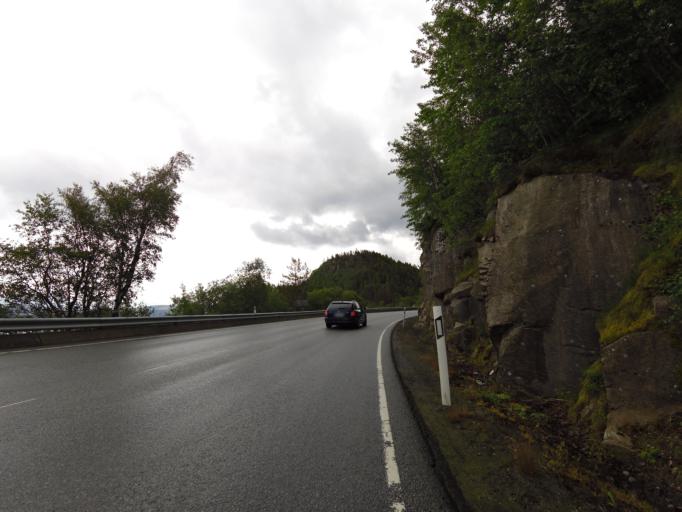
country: NO
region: Vest-Agder
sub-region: Farsund
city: Farsund
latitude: 58.0999
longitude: 6.8279
